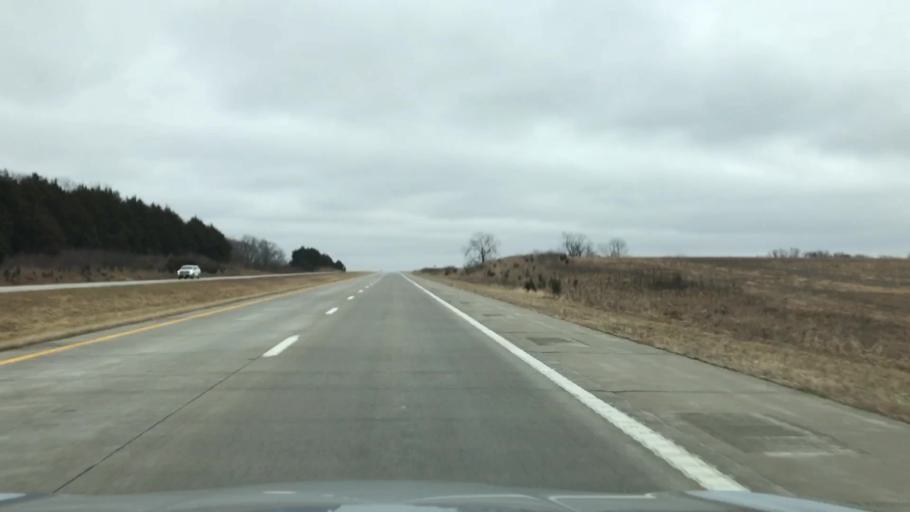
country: US
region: Missouri
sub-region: Caldwell County
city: Hamilton
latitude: 39.7351
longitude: -93.8622
